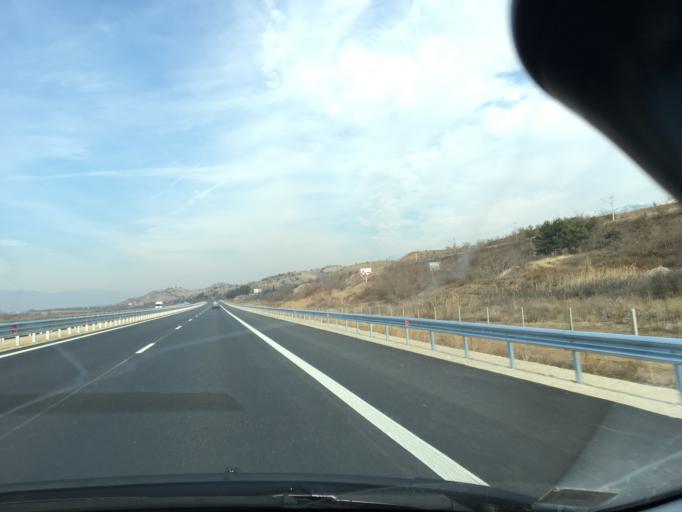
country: BG
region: Blagoevgrad
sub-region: Obshtina Sandanski
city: Sandanski
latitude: 41.5799
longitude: 23.2382
